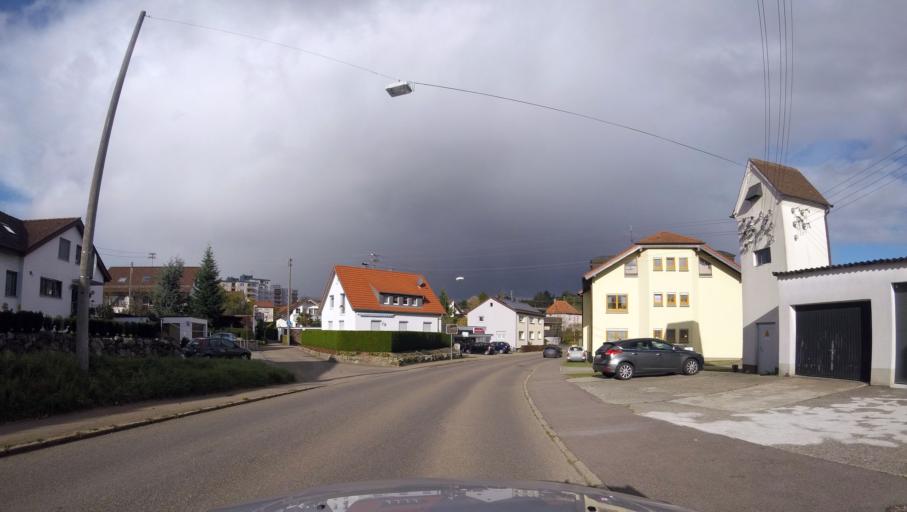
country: DE
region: Baden-Wuerttemberg
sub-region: Regierungsbezirk Stuttgart
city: Mutlangen
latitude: 48.8148
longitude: 9.7561
